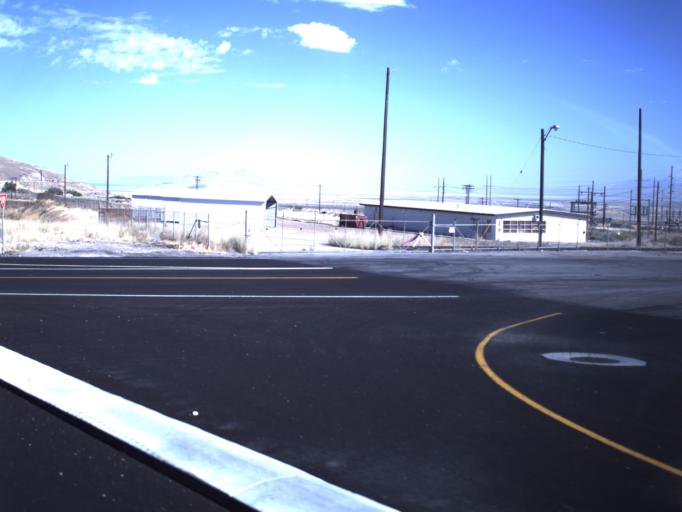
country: US
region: Utah
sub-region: Salt Lake County
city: Magna
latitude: 40.6618
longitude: -112.0875
